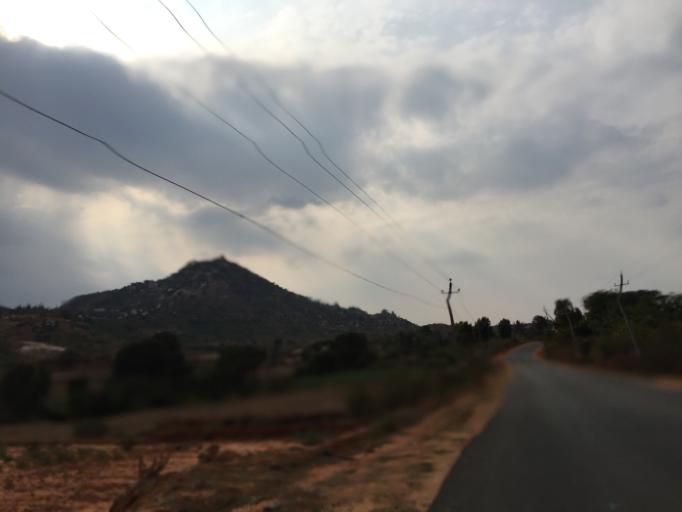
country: IN
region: Karnataka
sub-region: Chikkaballapur
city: Chik Ballapur
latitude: 13.5528
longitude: 77.7468
